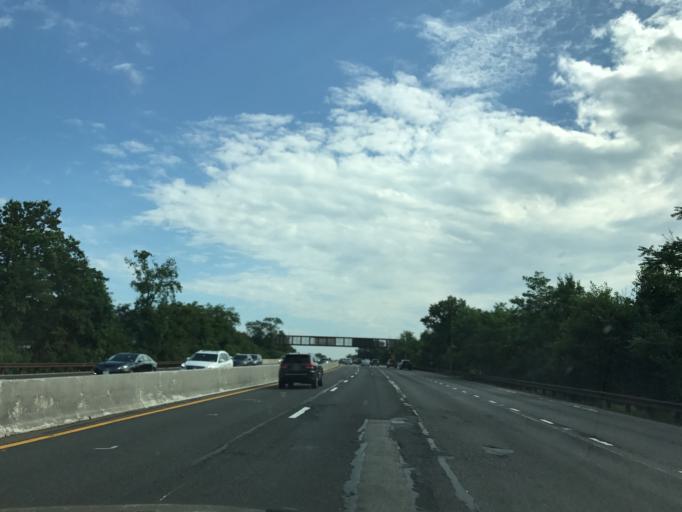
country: US
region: New Jersey
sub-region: Essex County
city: Irvington
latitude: 40.7411
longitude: -74.2155
